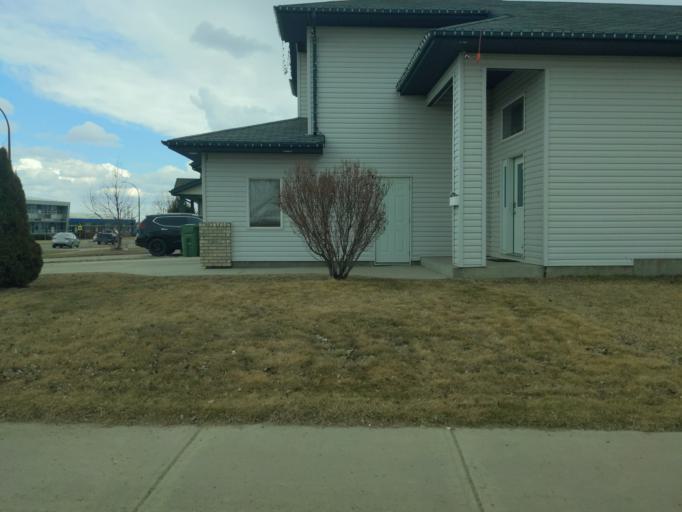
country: CA
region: Saskatchewan
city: Lloydminster
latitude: 53.2688
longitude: -110.0422
